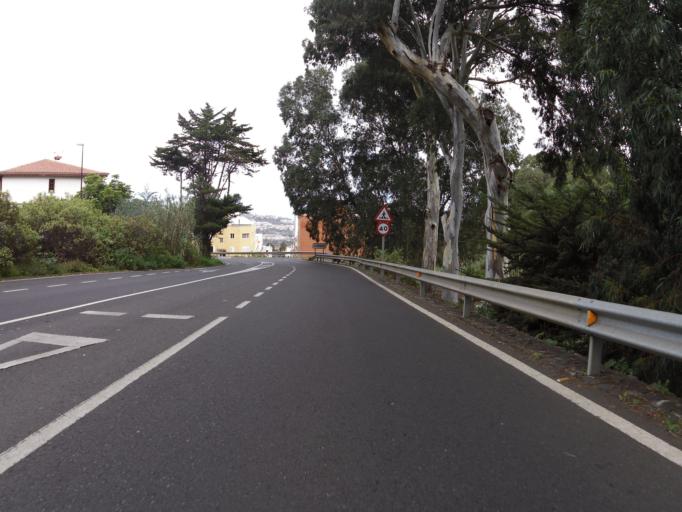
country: ES
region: Canary Islands
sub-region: Provincia de Las Palmas
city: Arucas
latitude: 28.0987
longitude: -15.5306
